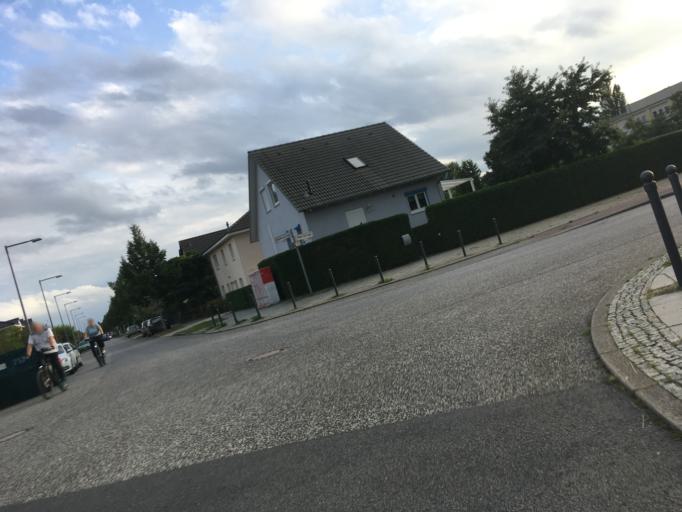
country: DE
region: Berlin
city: Johannisthal
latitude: 52.4384
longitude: 13.5109
